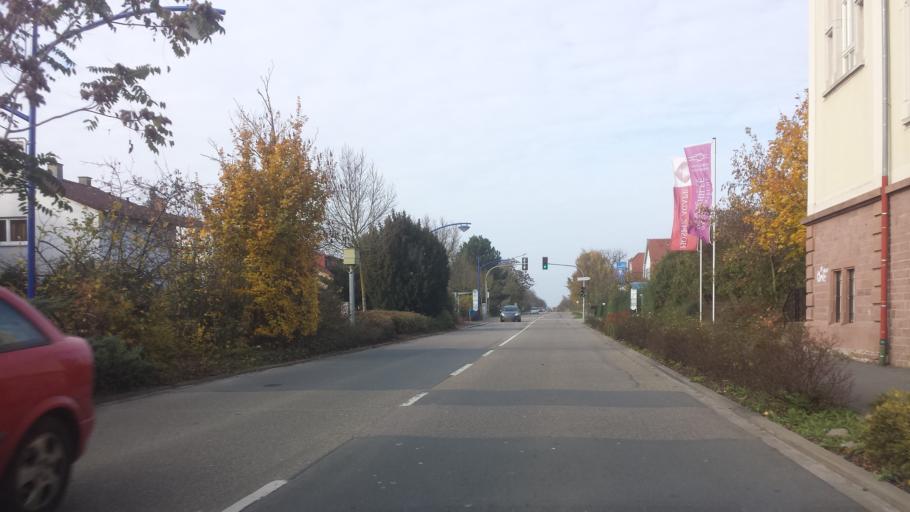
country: DE
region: Baden-Wuerttemberg
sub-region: Karlsruhe Region
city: Wiesloch
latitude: 49.2999
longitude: 8.6996
